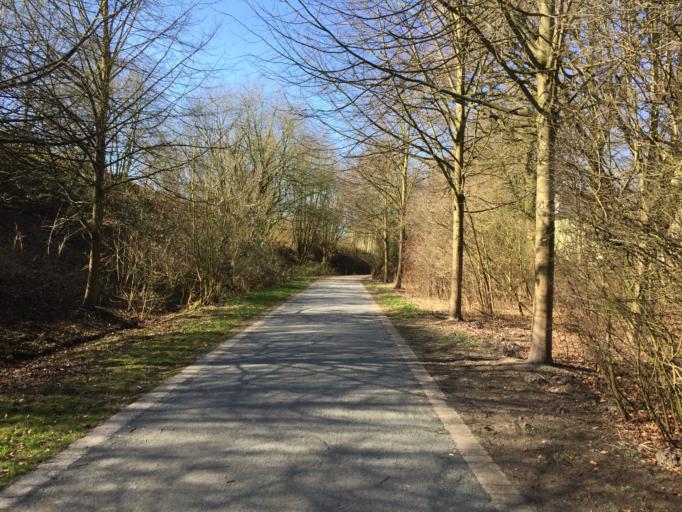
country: DE
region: Lower Saxony
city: Oldenburg
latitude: 53.1609
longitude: 8.2357
